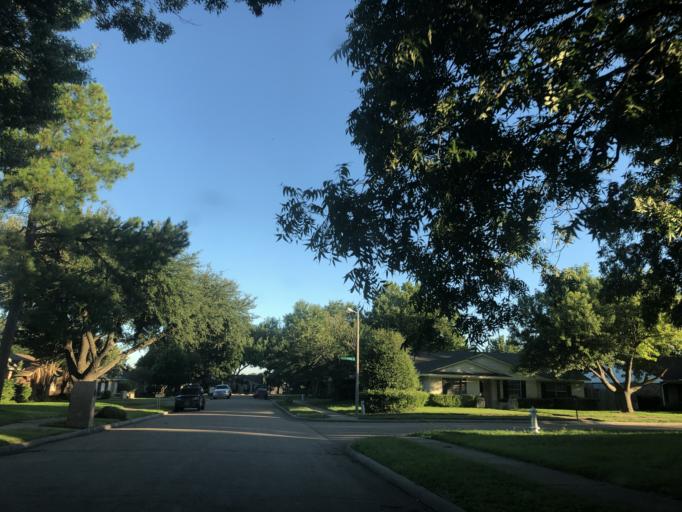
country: US
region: Texas
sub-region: Dallas County
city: Garland
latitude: 32.8367
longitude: -96.6404
